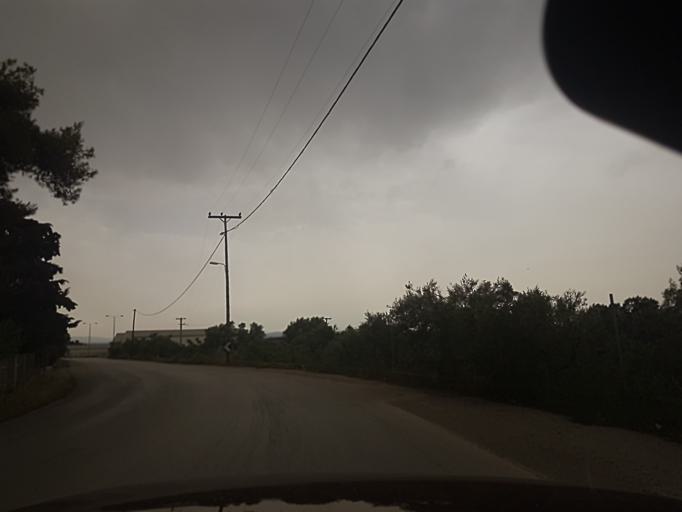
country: GR
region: Central Greece
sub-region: Nomos Evvoias
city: Vasilikon
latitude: 38.4390
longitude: 23.6684
